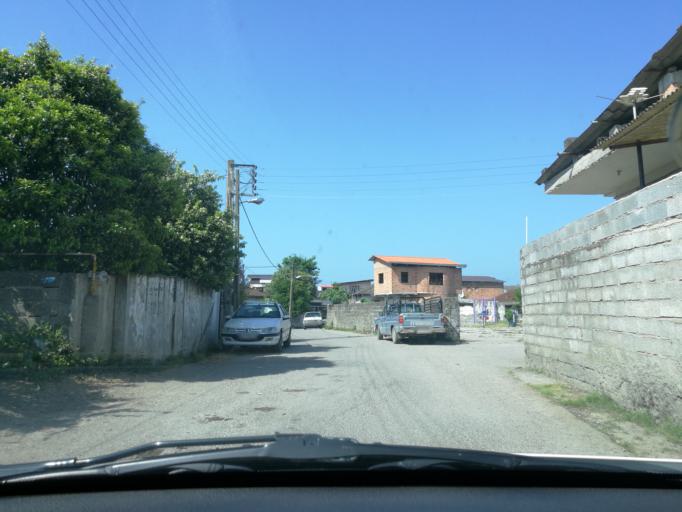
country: IR
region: Mazandaran
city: Chalus
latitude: 36.6683
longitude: 51.4320
